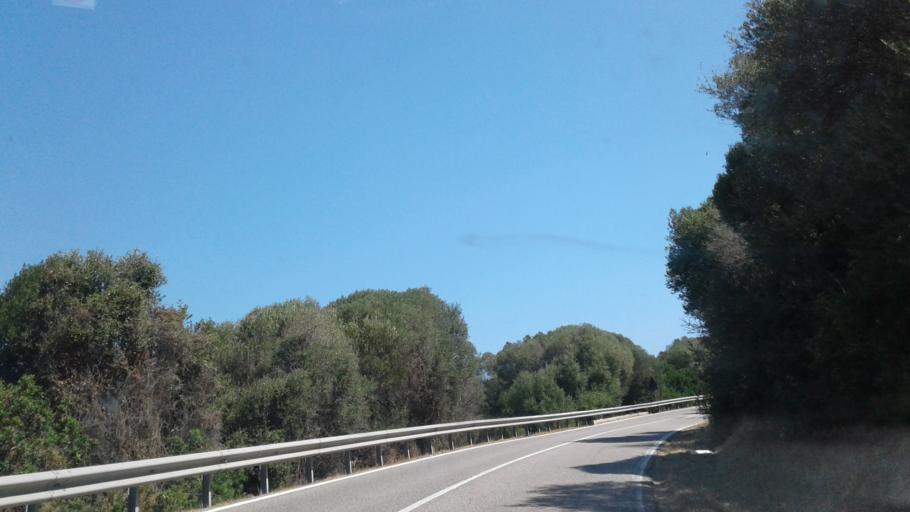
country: IT
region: Sardinia
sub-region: Provincia di Olbia-Tempio
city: Palau
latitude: 41.1664
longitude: 9.3160
